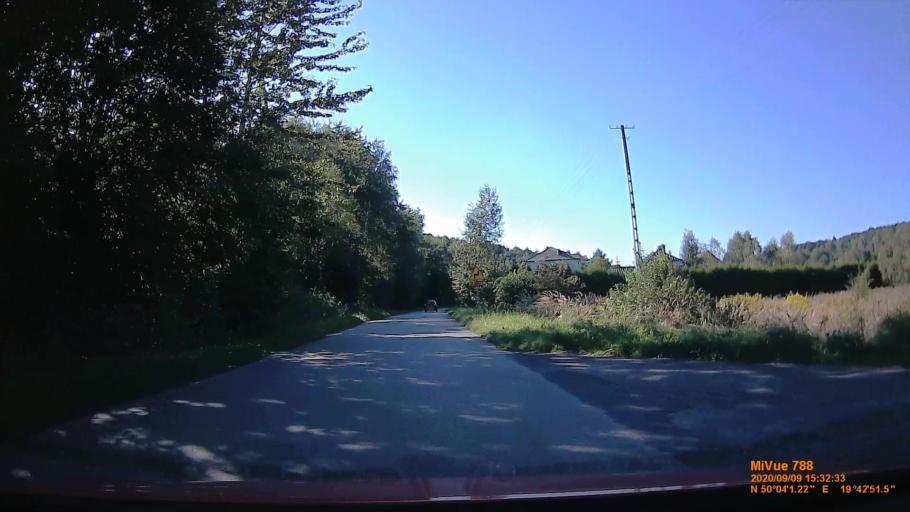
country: PL
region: Lesser Poland Voivodeship
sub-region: Powiat krakowski
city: Mnikow
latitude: 50.0670
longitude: 19.7143
